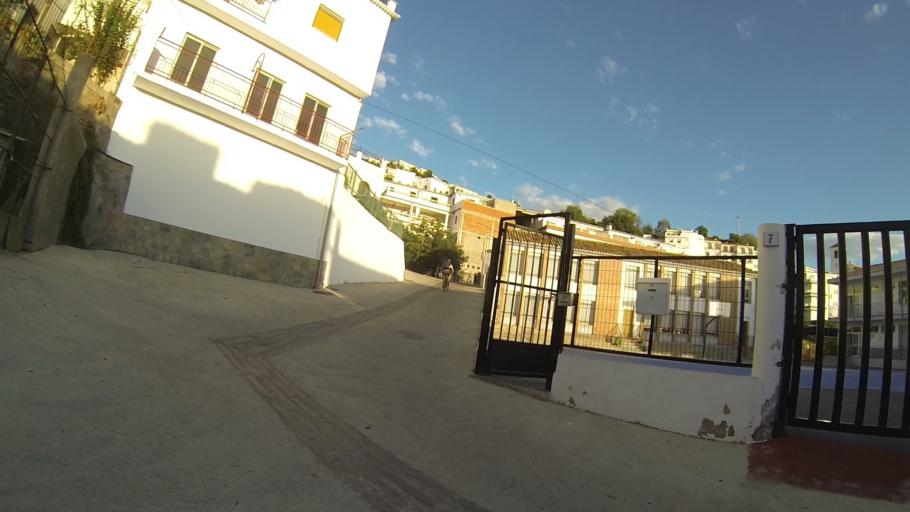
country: ES
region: Andalusia
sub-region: Provincia de Granada
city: Berchules
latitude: 36.9809
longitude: -3.1551
